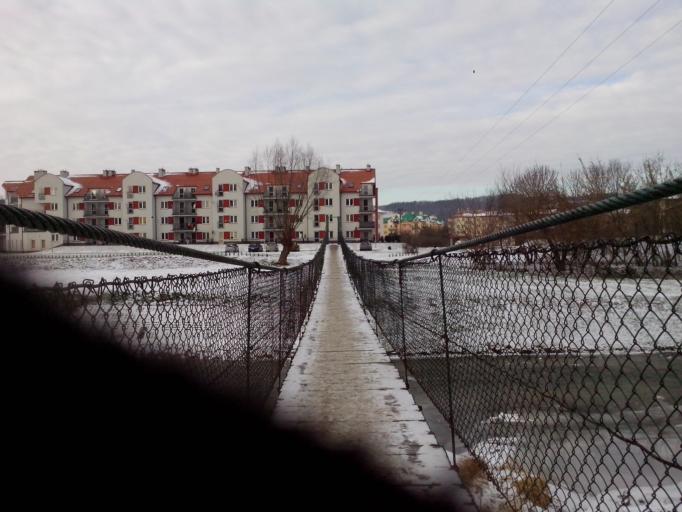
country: PL
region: Subcarpathian Voivodeship
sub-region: Powiat strzyzowski
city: Strzyzow
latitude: 49.8654
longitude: 21.8011
